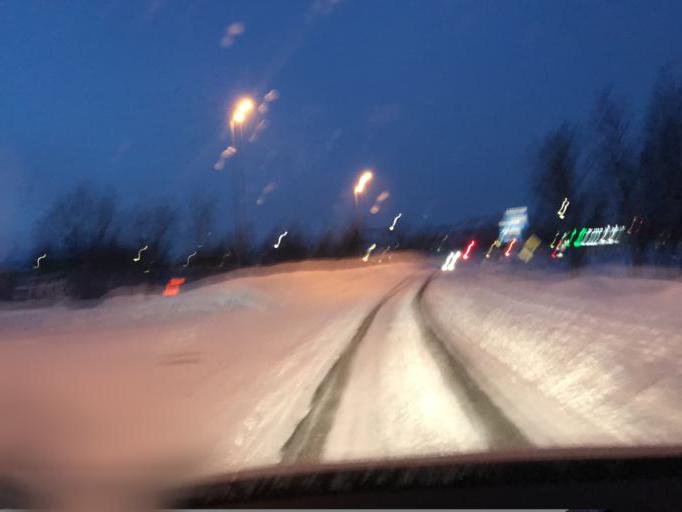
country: SE
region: Norrbotten
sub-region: Kiruna Kommun
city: Kiruna
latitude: 67.8457
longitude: 20.2308
